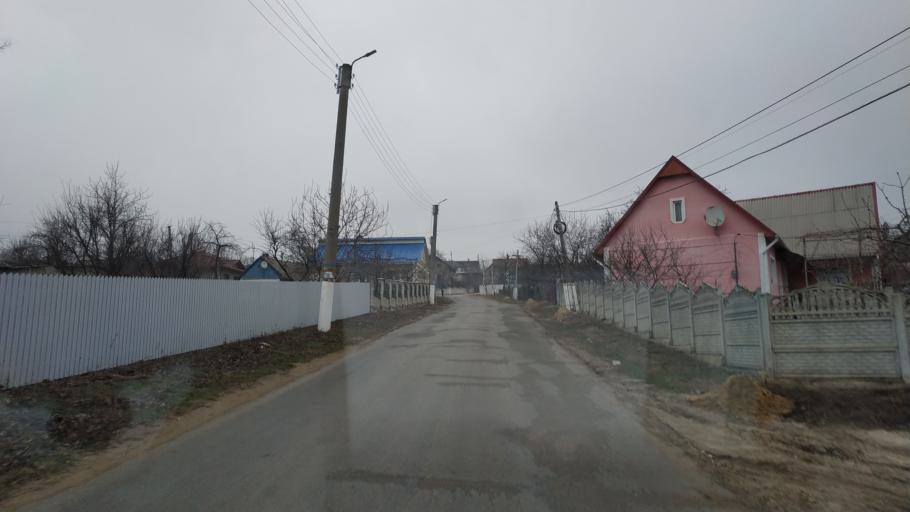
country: MD
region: Laloveni
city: Ialoveni
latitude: 46.8878
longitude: 28.6882
